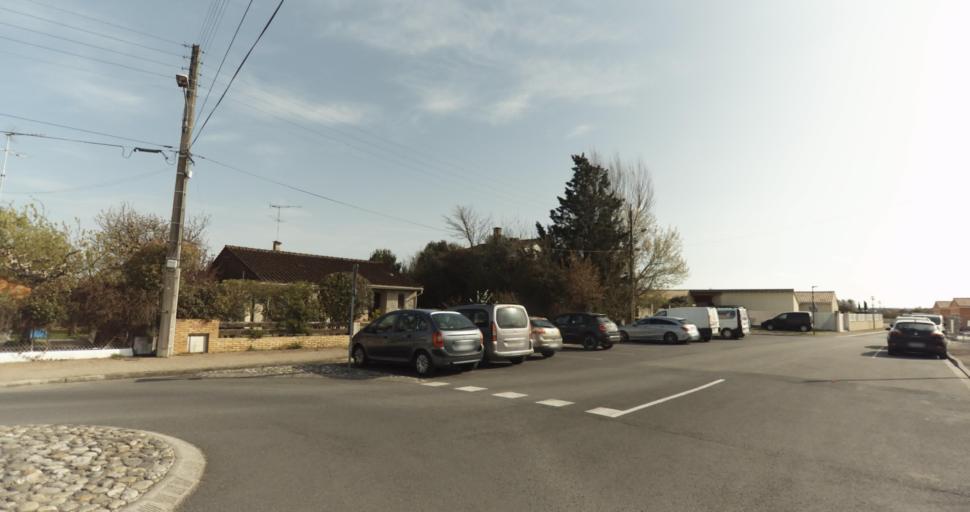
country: FR
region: Midi-Pyrenees
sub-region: Departement du Tarn
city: Saint-Sulpice-la-Pointe
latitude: 43.7743
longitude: 1.6914
